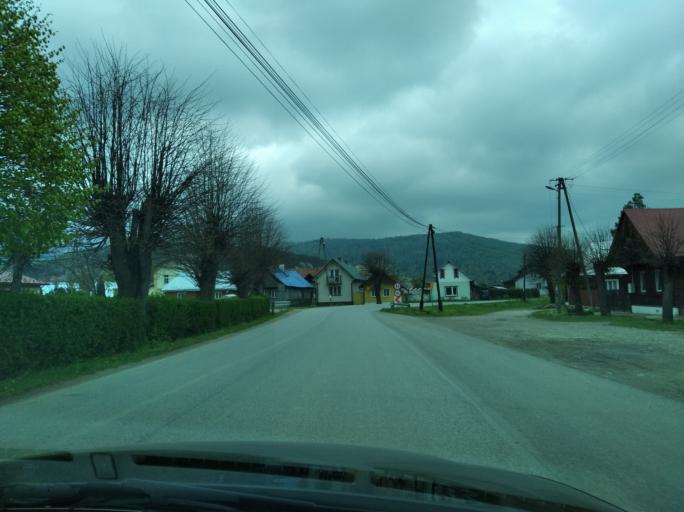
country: PL
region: Subcarpathian Voivodeship
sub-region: Powiat sanocki
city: Sanok
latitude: 49.6191
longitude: 22.2728
